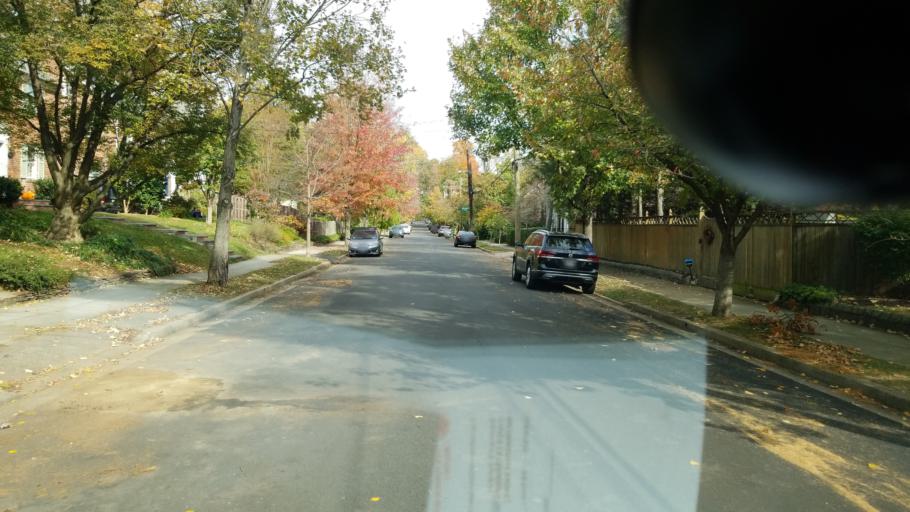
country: US
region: Maryland
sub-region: Montgomery County
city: Chevy Chase
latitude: 38.9741
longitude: -77.0597
